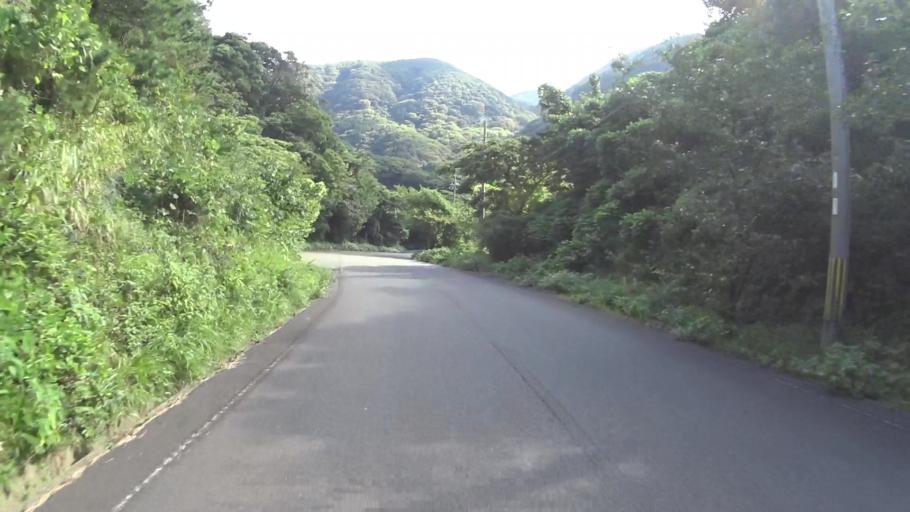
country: JP
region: Kyoto
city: Miyazu
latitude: 35.7732
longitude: 135.2246
